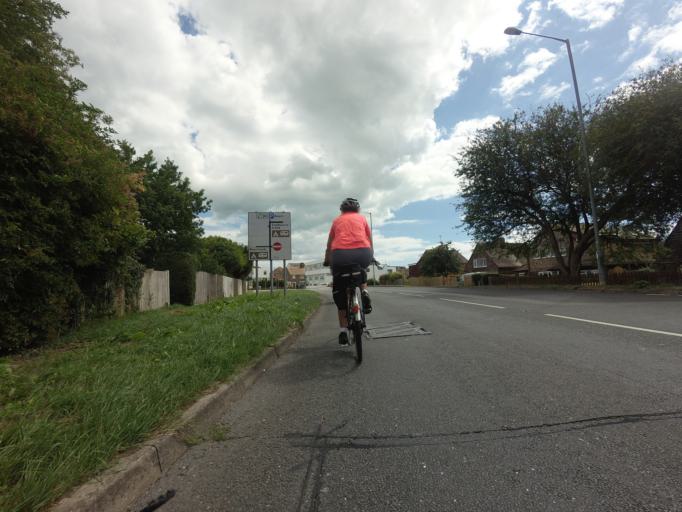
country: GB
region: England
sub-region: East Sussex
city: Pevensey
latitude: 50.8137
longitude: 0.3510
